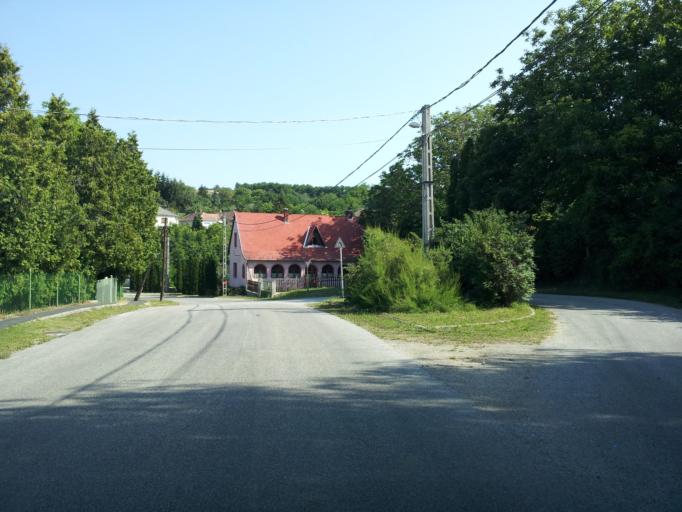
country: HU
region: Zala
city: Cserszegtomaj
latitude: 46.8435
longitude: 17.2188
